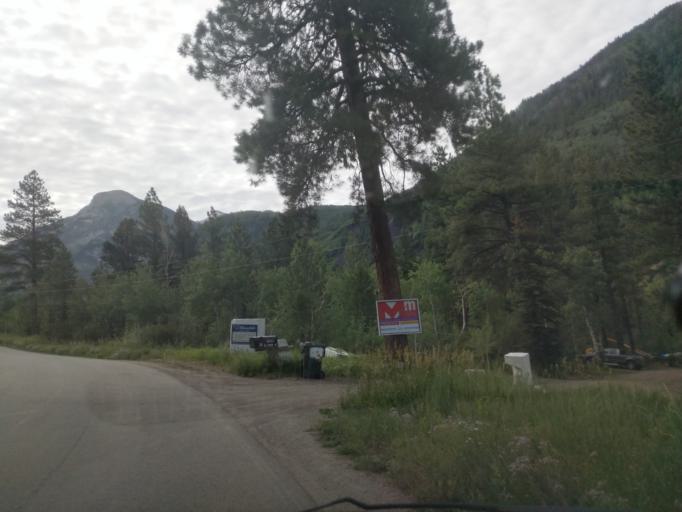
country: US
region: Colorado
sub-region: Gunnison County
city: Crested Butte
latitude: 39.0705
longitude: -107.1973
